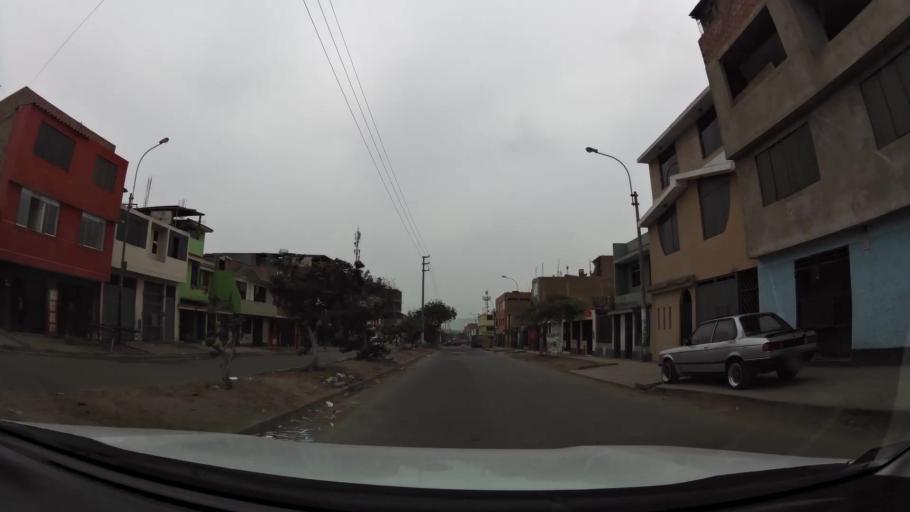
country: PE
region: Lima
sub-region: Lima
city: Surco
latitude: -12.1722
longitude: -76.9668
